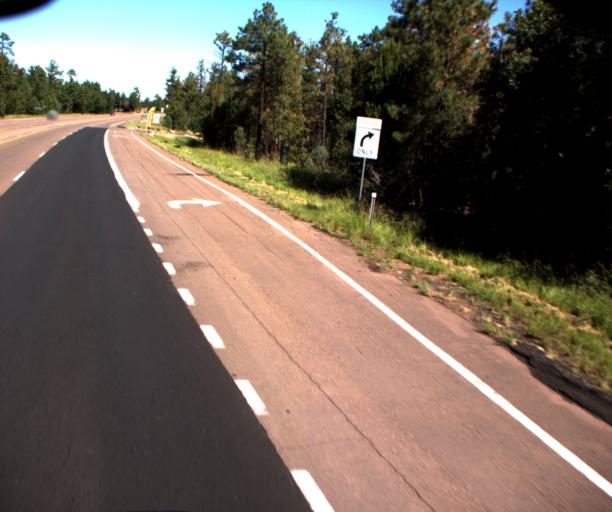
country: US
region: Arizona
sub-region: Navajo County
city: Lake of the Woods
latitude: 34.1801
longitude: -110.0126
